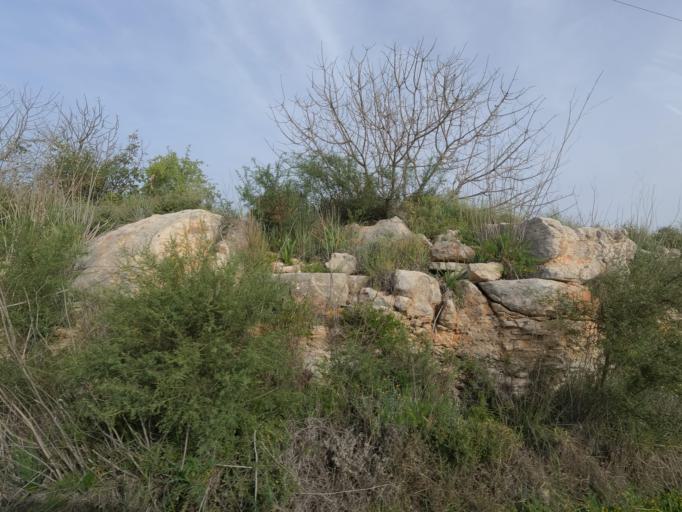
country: CY
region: Pafos
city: Pegeia
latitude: 34.9461
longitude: 32.3771
